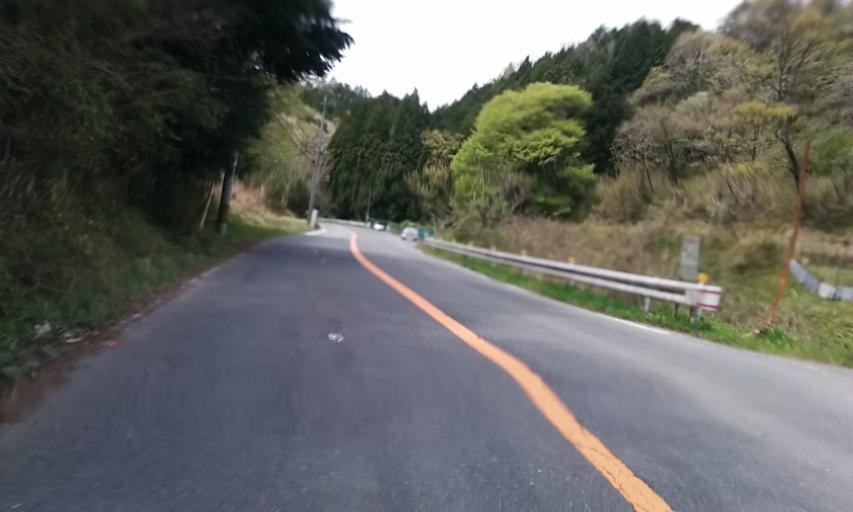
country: JP
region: Kyoto
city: Kameoka
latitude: 34.9463
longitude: 135.5956
